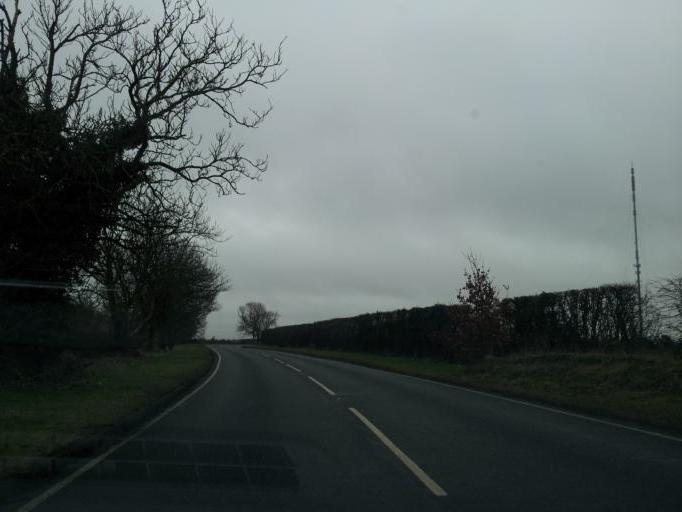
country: GB
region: England
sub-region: Essex
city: Mistley
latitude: 51.9280
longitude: 1.0805
